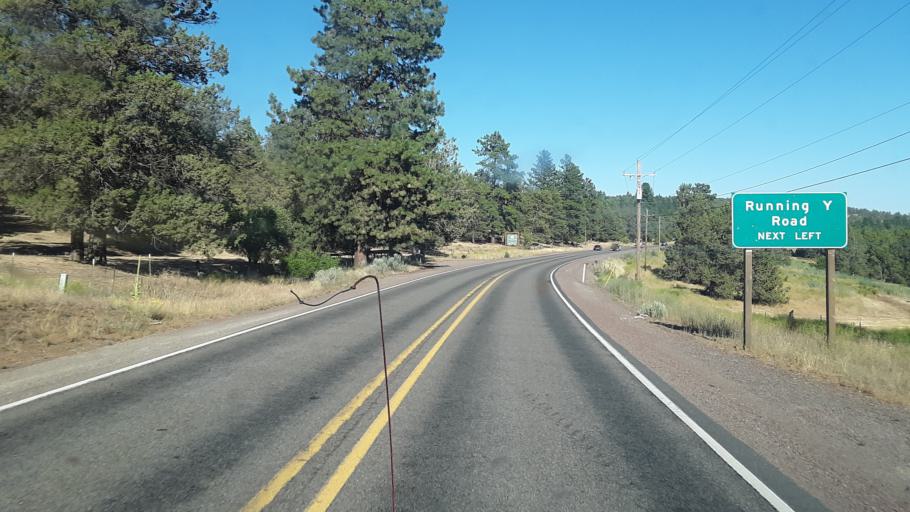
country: US
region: Oregon
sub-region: Klamath County
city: Klamath Falls
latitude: 42.2747
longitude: -121.8919
